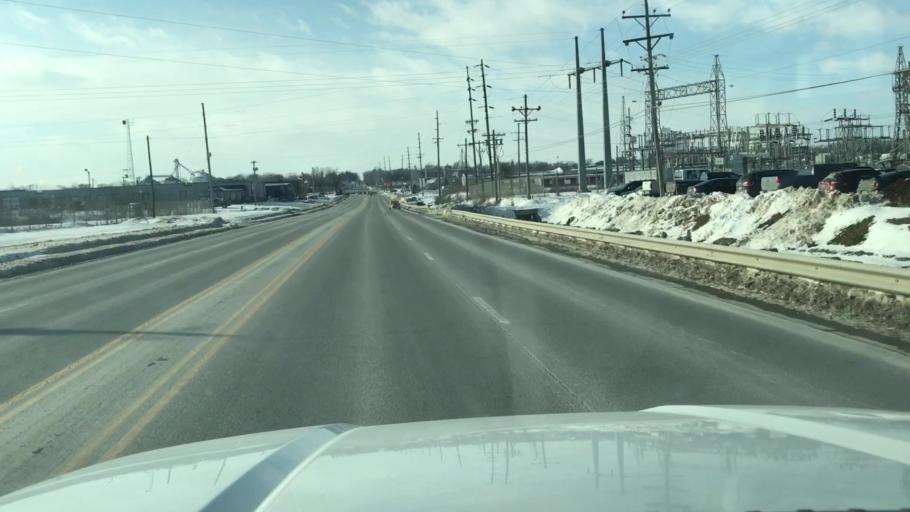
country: US
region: Missouri
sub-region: Nodaway County
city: Maryville
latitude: 40.3452
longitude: -94.8460
